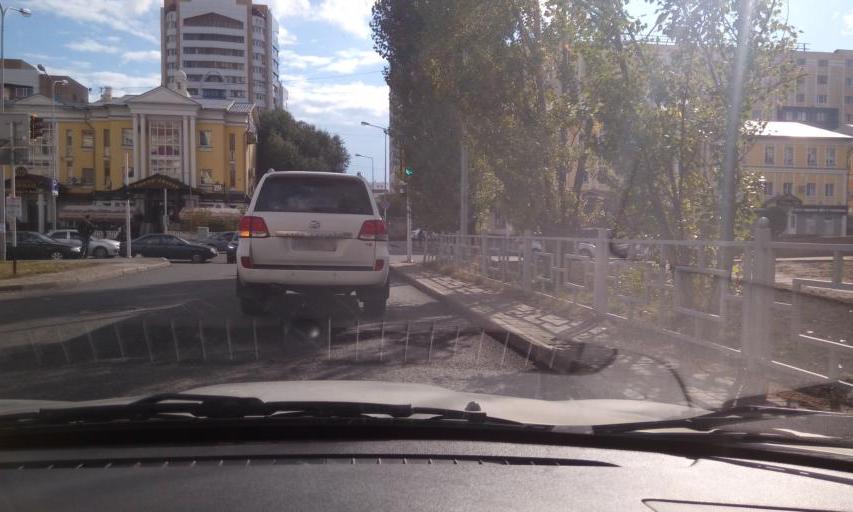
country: KZ
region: Astana Qalasy
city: Astana
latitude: 51.1637
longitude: 71.4322
